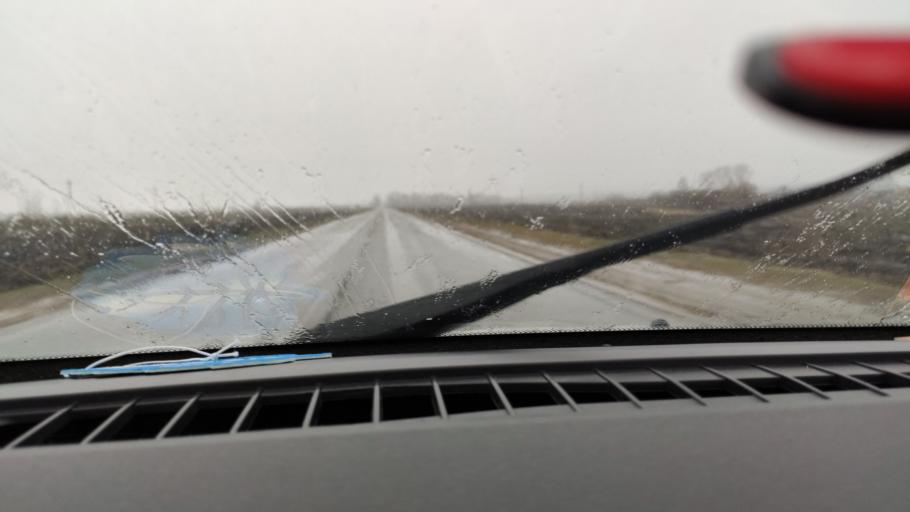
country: RU
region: Tatarstan
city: Cheremshan
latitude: 54.7141
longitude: 51.2025
